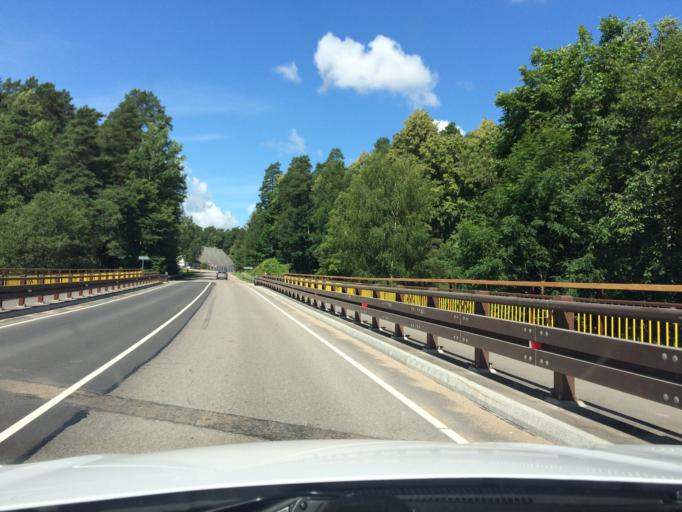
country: LV
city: Tervete
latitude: 56.4787
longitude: 23.3851
